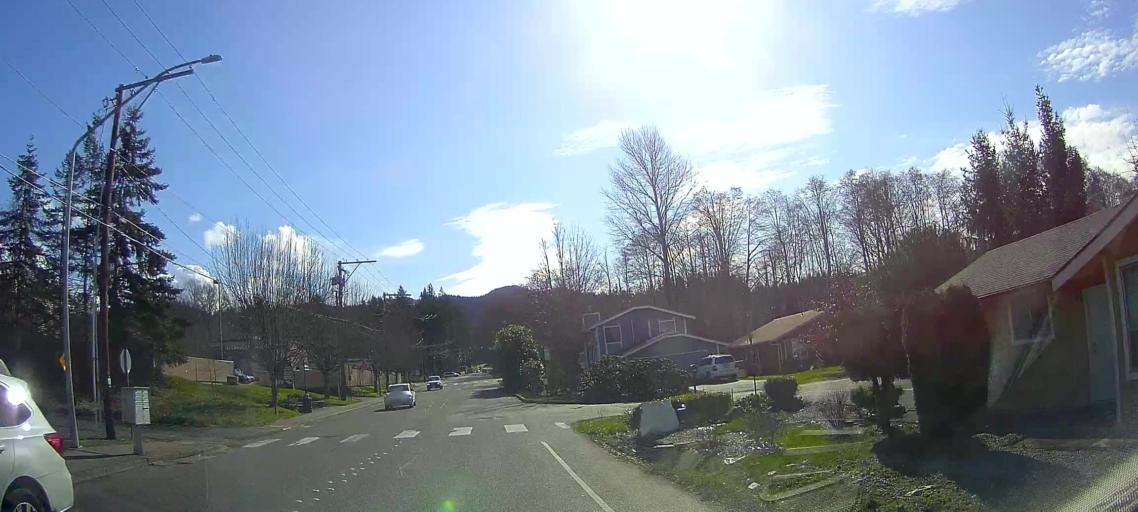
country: US
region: Washington
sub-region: Whatcom County
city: Bellingham
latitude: 48.7159
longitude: -122.4782
